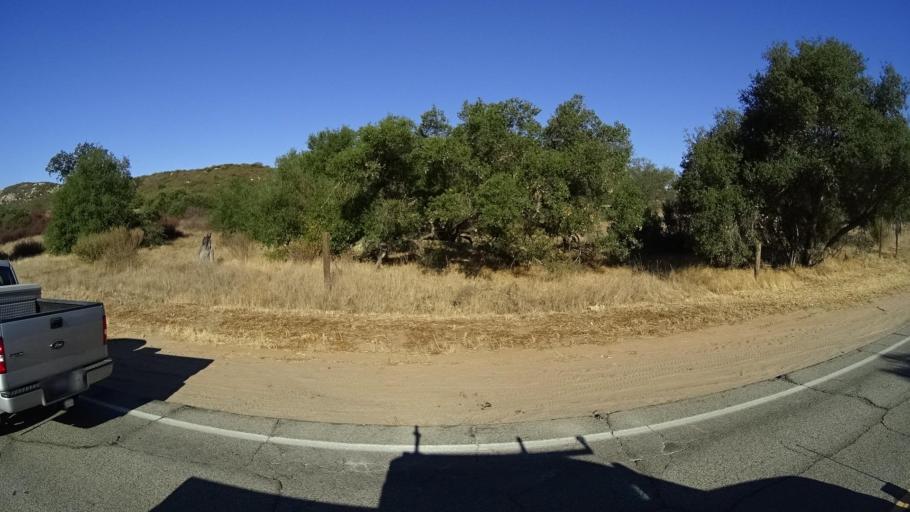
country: US
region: California
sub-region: San Diego County
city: San Diego Country Estates
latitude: 32.9599
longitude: -116.8365
